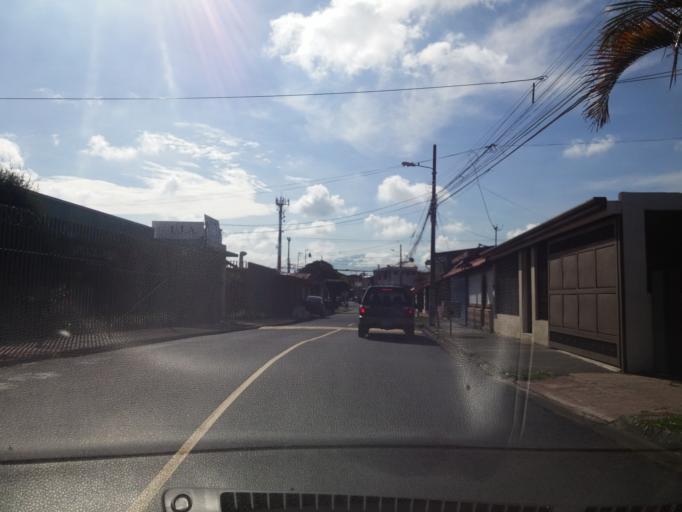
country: CR
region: Heredia
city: San Francisco
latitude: 9.9976
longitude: -84.1292
